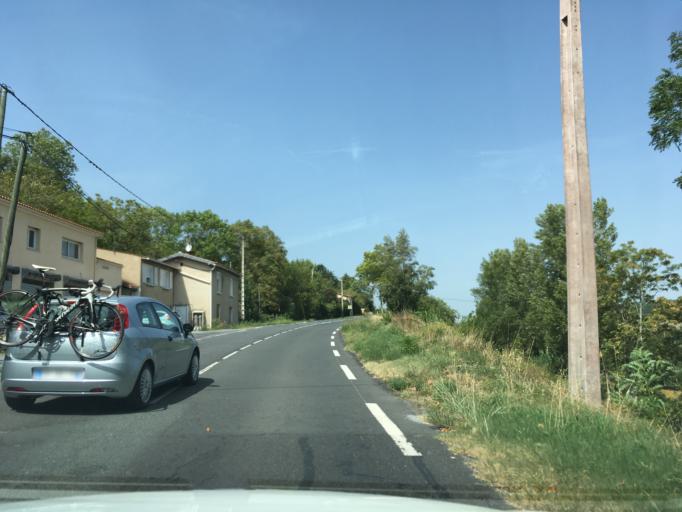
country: FR
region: Midi-Pyrenees
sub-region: Departement du Tarn
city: Castres
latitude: 43.6139
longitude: 2.2204
